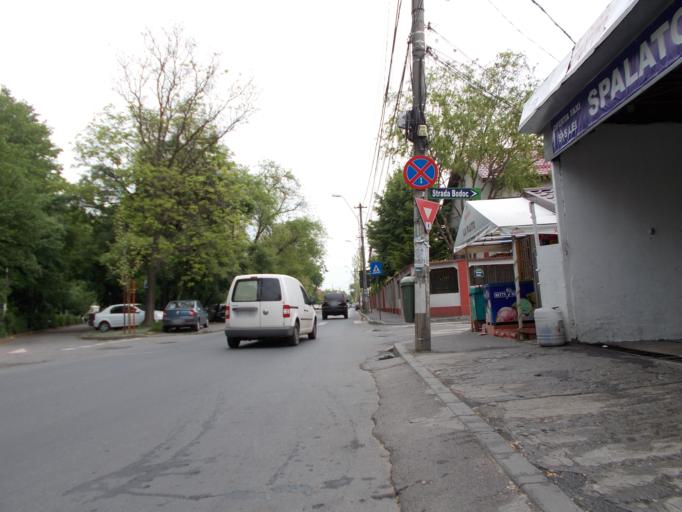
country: RO
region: Bucuresti
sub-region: Municipiul Bucuresti
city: Bucuresti
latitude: 44.3906
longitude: 26.0964
